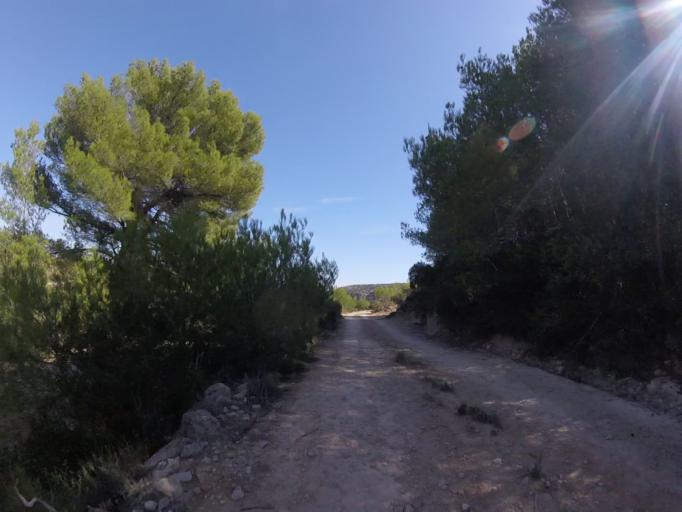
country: ES
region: Valencia
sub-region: Provincia de Castello
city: Sarratella
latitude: 40.2730
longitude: 0.0353
